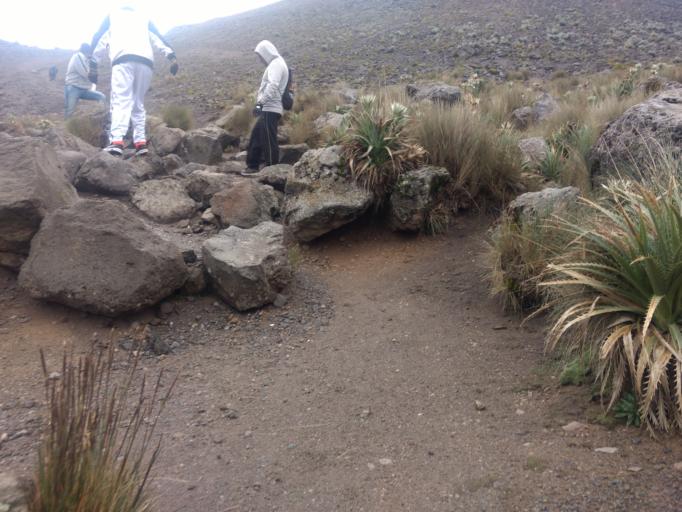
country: MX
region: Mexico
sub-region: Tenango del Valle
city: Santa Cruz Pueblo Nuevo (Pueblo Nuevo)
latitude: 19.1104
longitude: -99.7526
